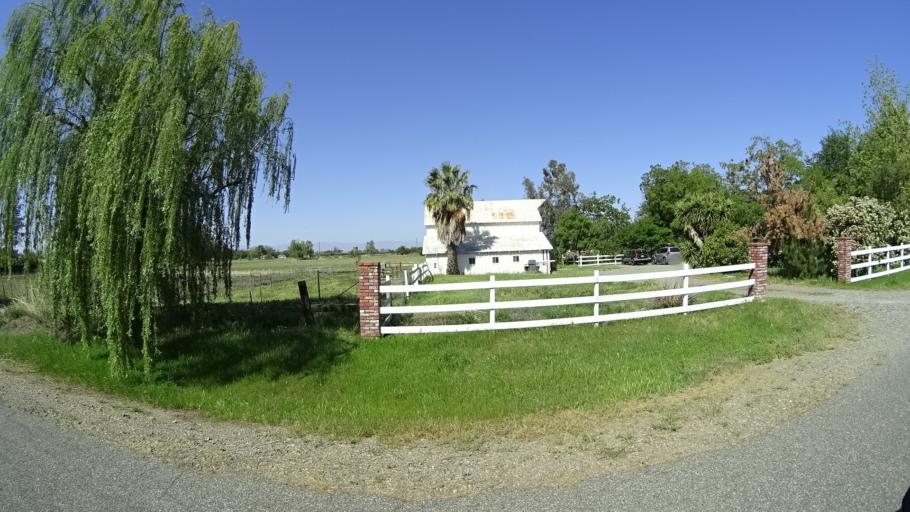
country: US
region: California
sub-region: Glenn County
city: Orland
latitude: 39.7246
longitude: -122.1924
